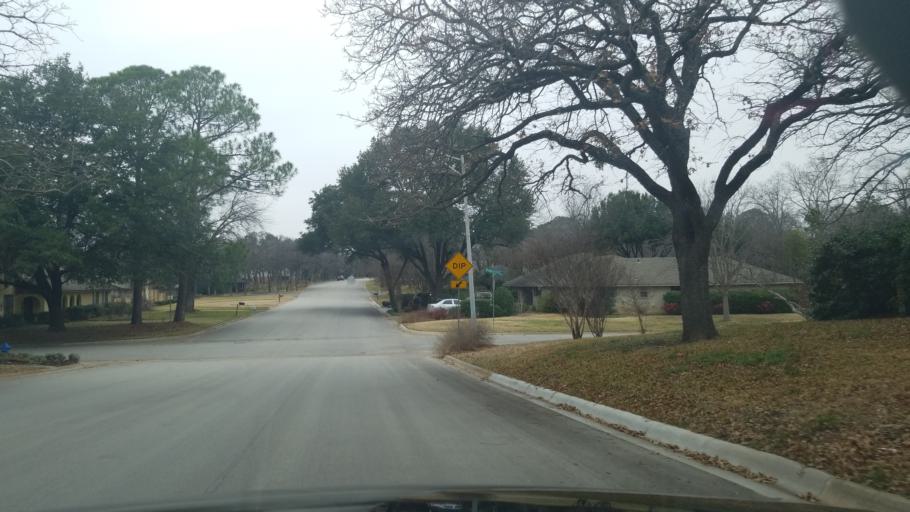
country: US
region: Texas
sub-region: Denton County
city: Denton
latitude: 33.1871
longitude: -97.1162
